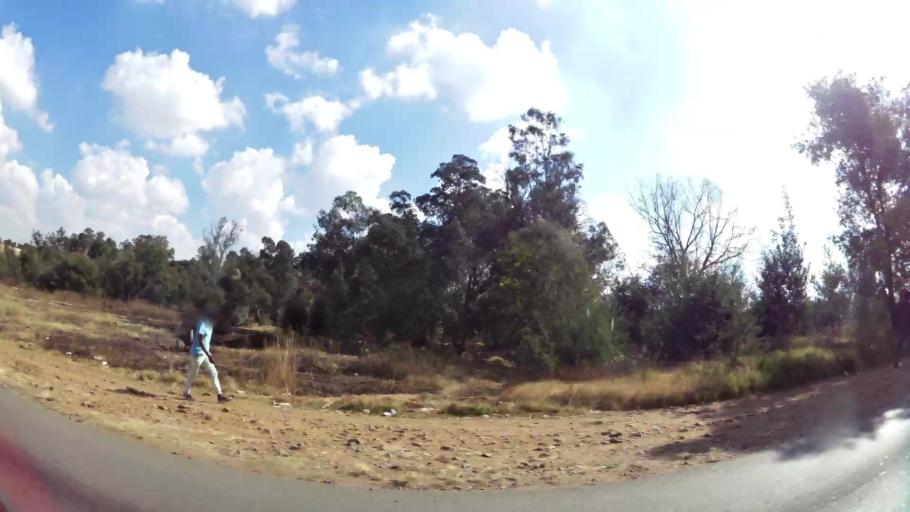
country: ZA
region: Gauteng
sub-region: City of Johannesburg Metropolitan Municipality
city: Roodepoort
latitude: -26.1781
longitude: 27.8711
